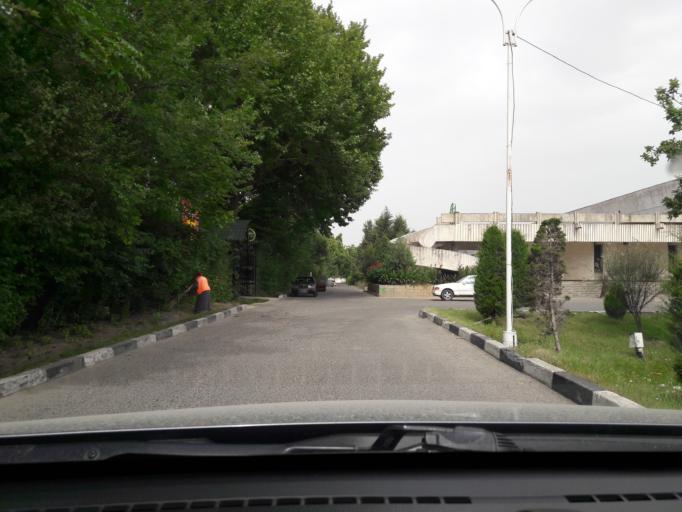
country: TJ
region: Dushanbe
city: Dushanbe
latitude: 38.5817
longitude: 68.7640
